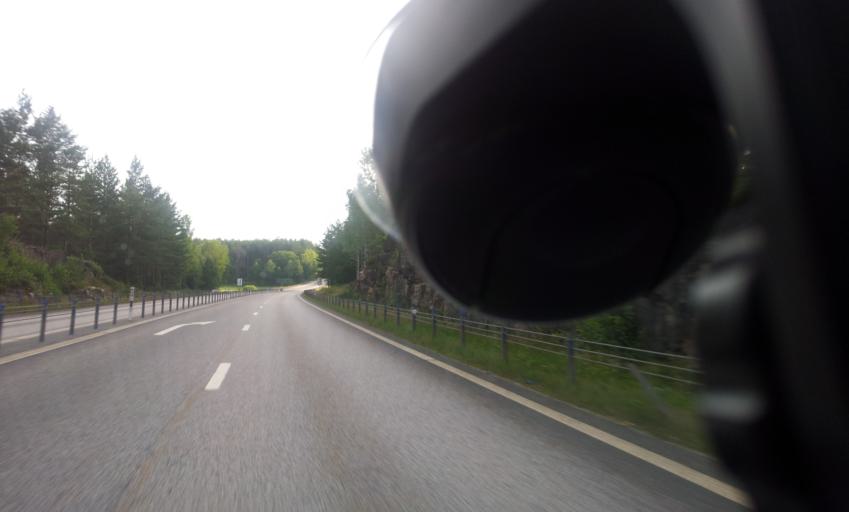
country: SE
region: OEstergoetland
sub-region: Valdemarsviks Kommun
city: Valdemarsvik
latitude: 58.1310
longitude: 16.5325
